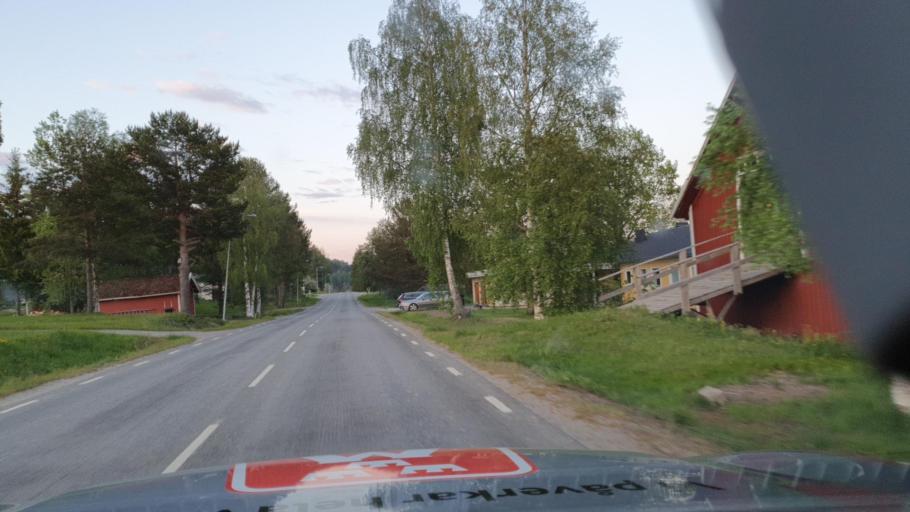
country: SE
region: Vaesternorrland
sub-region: OErnskoeldsviks Kommun
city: Kopmanholmen
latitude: 63.2328
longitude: 18.5709
